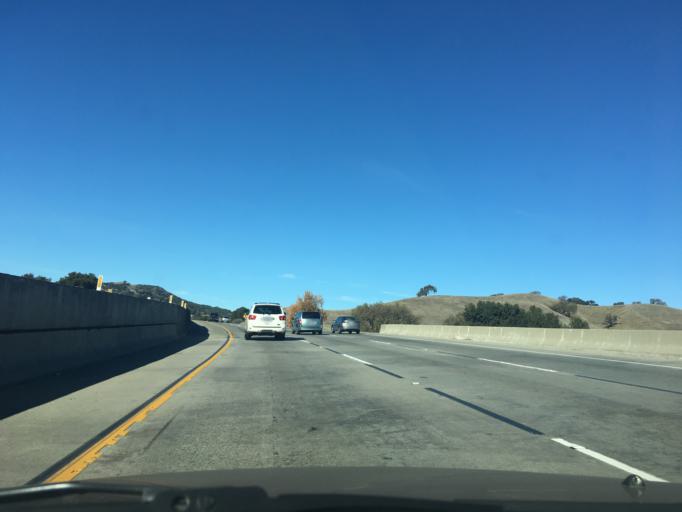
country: US
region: California
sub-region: Alameda County
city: Pleasanton
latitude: 37.5930
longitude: -121.8704
